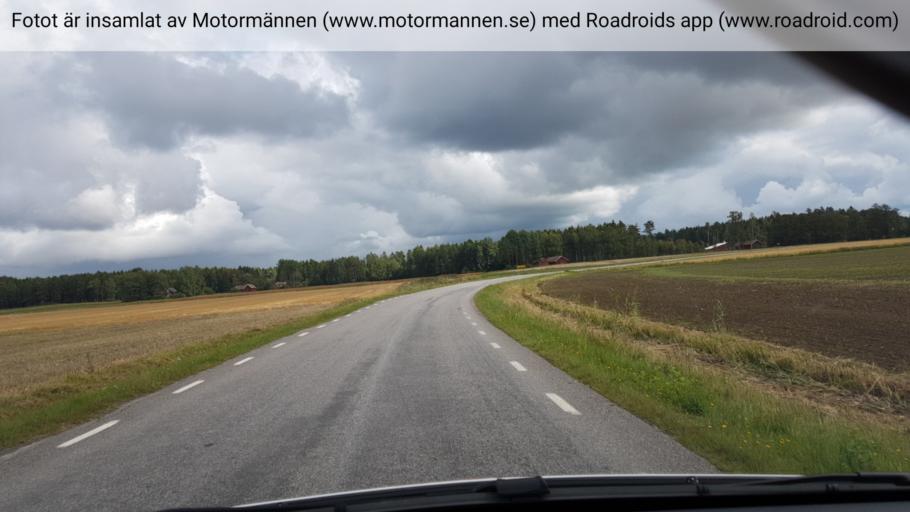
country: SE
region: Vaestra Goetaland
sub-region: Lidkopings Kommun
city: Vinninga
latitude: 58.3829
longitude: 13.3077
